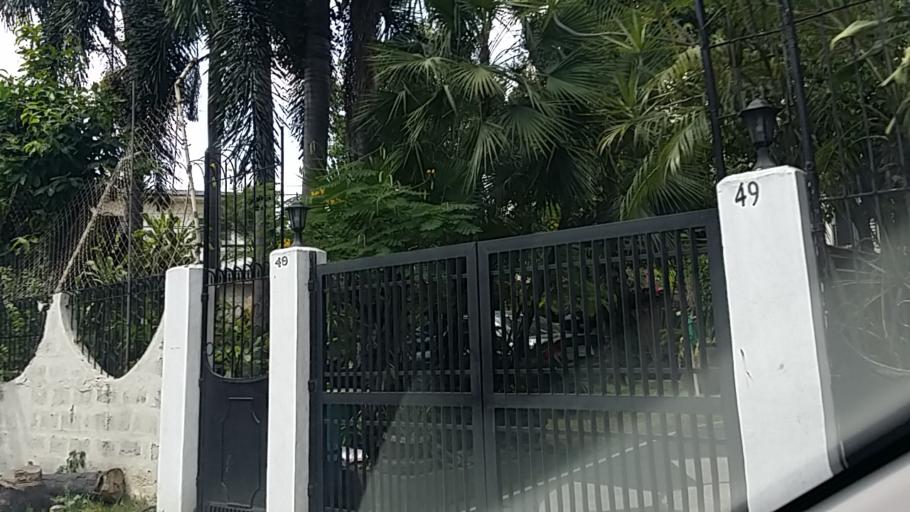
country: PH
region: Metro Manila
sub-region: Mandaluyong
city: Mandaluyong City
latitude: 14.5759
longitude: 121.0470
